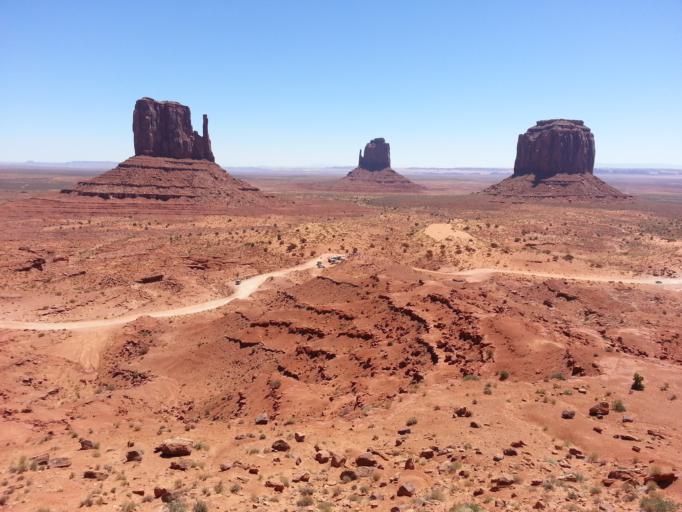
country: US
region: Arizona
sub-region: Navajo County
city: Kayenta
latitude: 36.9831
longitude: -110.1117
